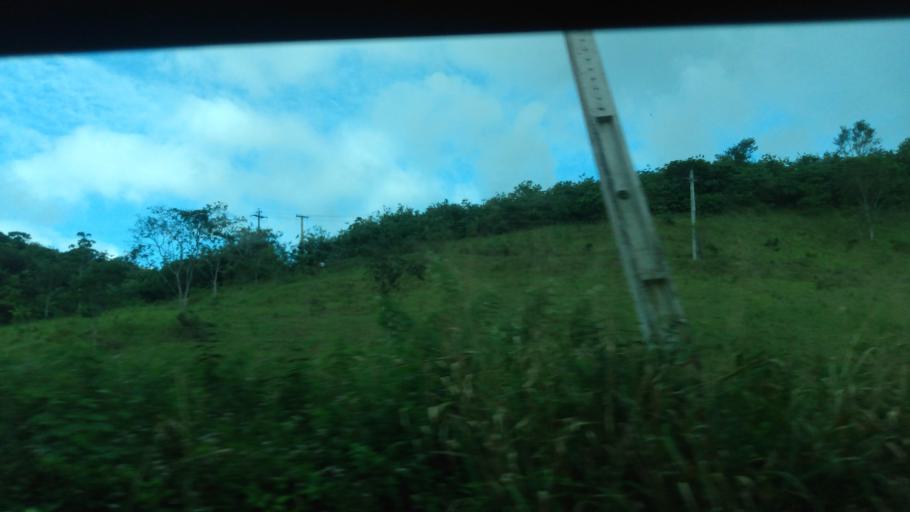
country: BR
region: Pernambuco
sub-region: Quipapa
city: Quipapa
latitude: -8.7905
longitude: -35.9795
